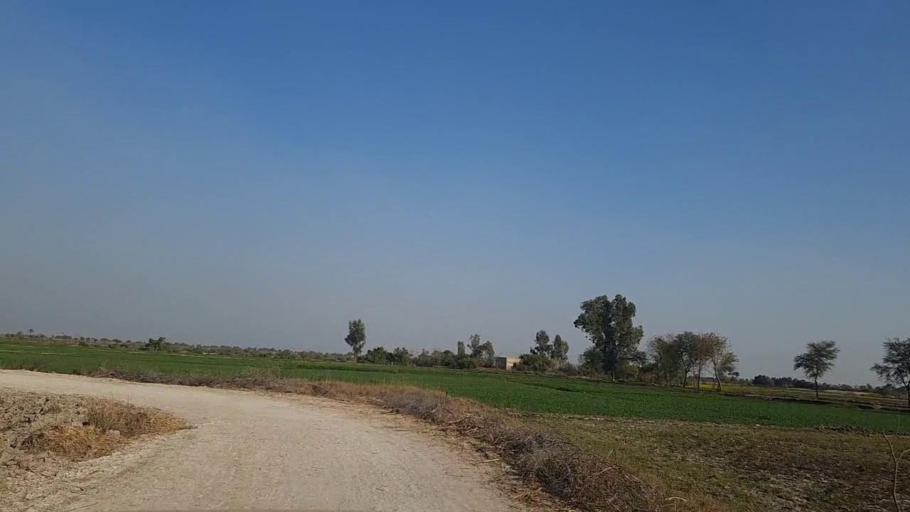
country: PK
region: Sindh
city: Daur
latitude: 26.3207
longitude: 68.1786
